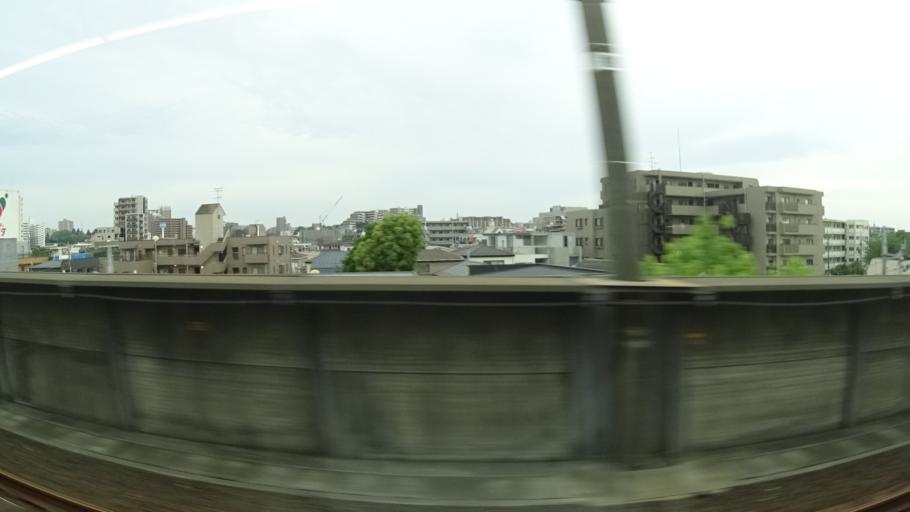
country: JP
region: Saitama
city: Kawaguchi
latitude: 35.7900
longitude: 139.7000
